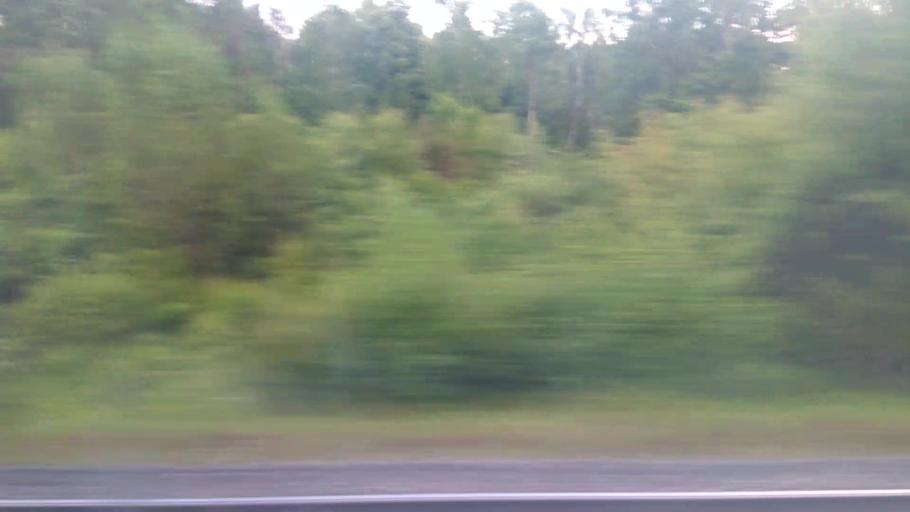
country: RU
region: Moskovskaya
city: Mikhnevo
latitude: 55.0777
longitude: 37.9776
